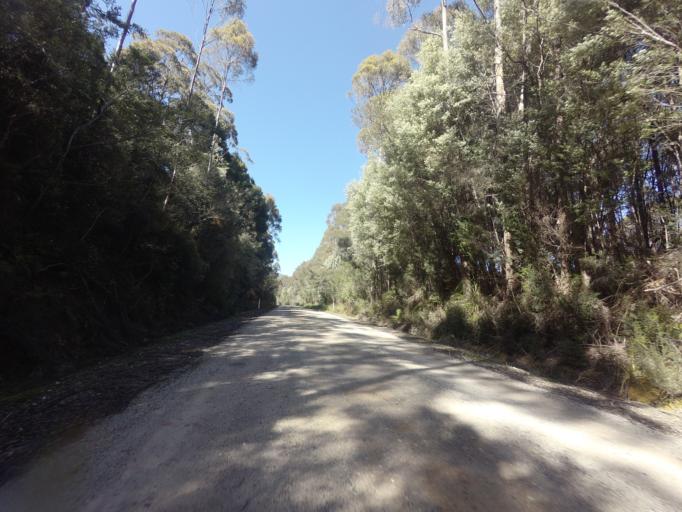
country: AU
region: Tasmania
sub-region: Huon Valley
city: Geeveston
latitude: -43.0125
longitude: 146.3640
